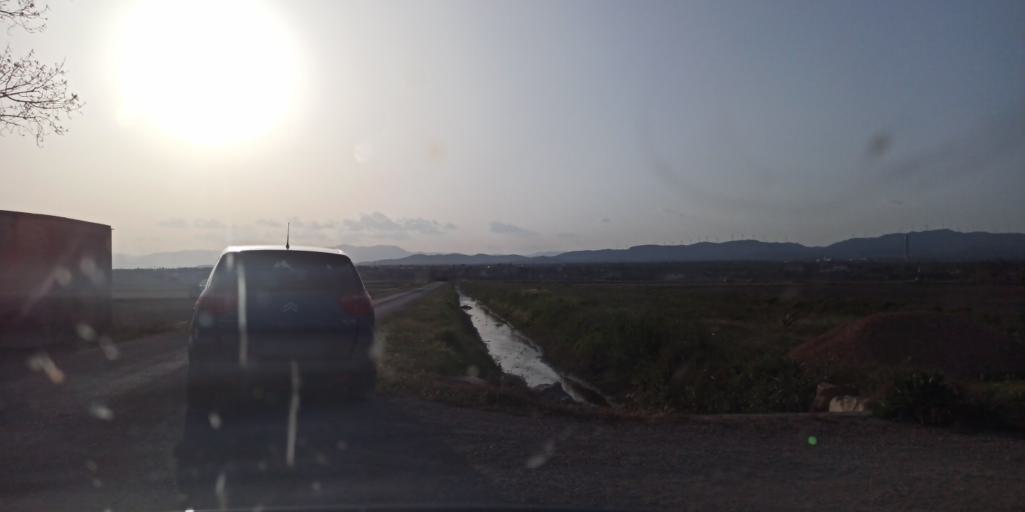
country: ES
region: Catalonia
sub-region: Provincia de Tarragona
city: L'Ampolla
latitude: 40.7852
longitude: 0.6969
